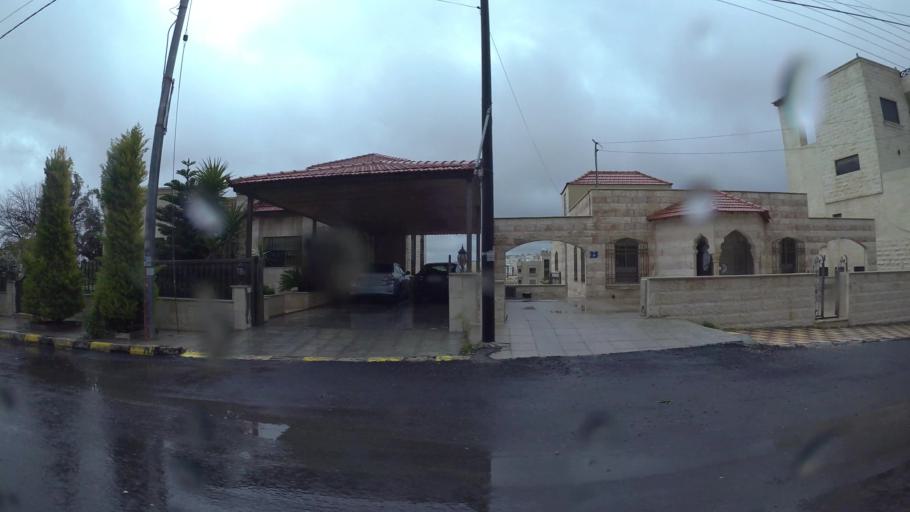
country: JO
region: Amman
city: Al Jubayhah
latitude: 32.0428
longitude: 35.8876
